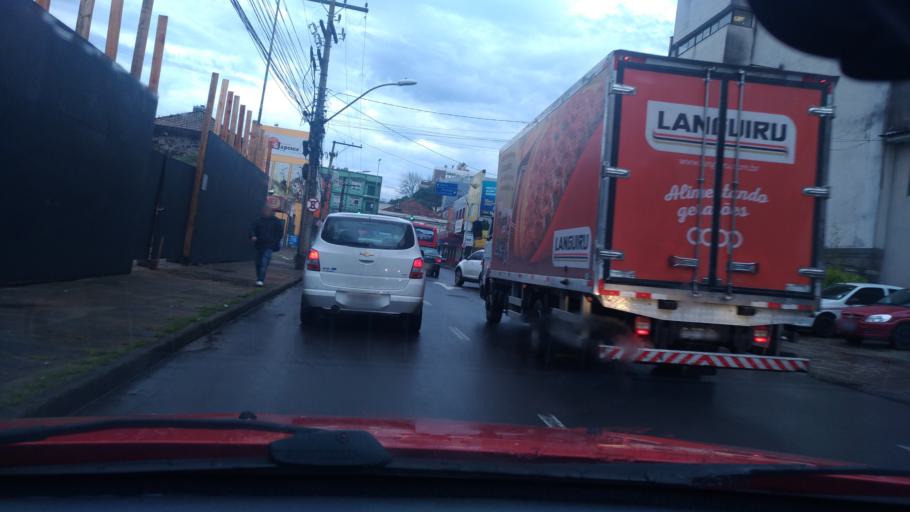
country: BR
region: Rio Grande do Sul
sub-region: Porto Alegre
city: Porto Alegre
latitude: -30.0120
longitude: -51.1619
